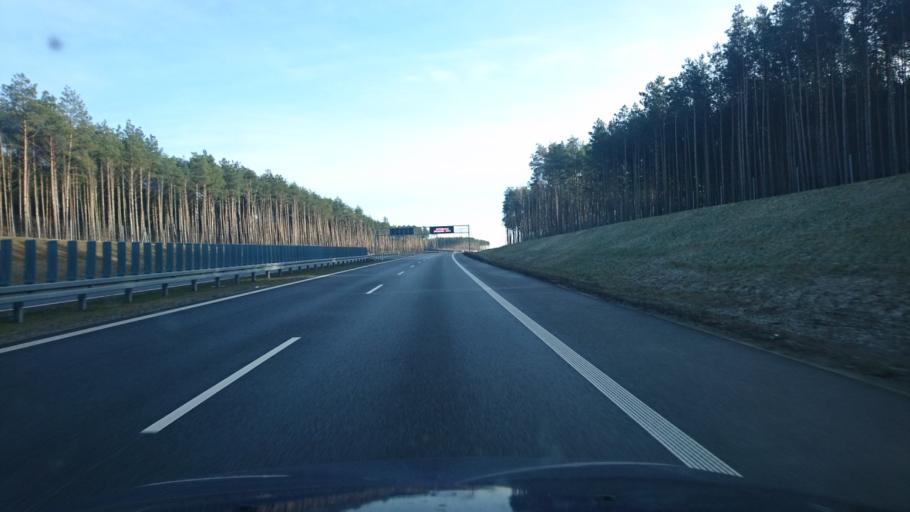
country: PL
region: Greater Poland Voivodeship
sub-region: Powiat kepinski
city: Kepno
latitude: 51.3291
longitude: 17.9793
